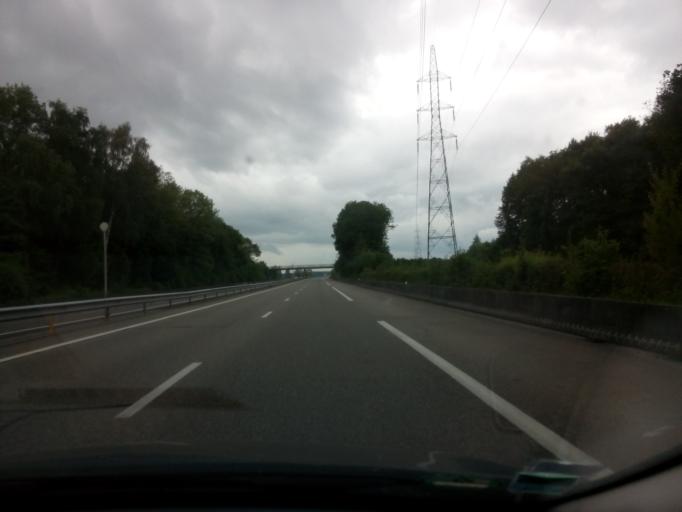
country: FR
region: Alsace
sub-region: Departement du Bas-Rhin
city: Drusenheim
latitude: 48.7845
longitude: 7.9599
